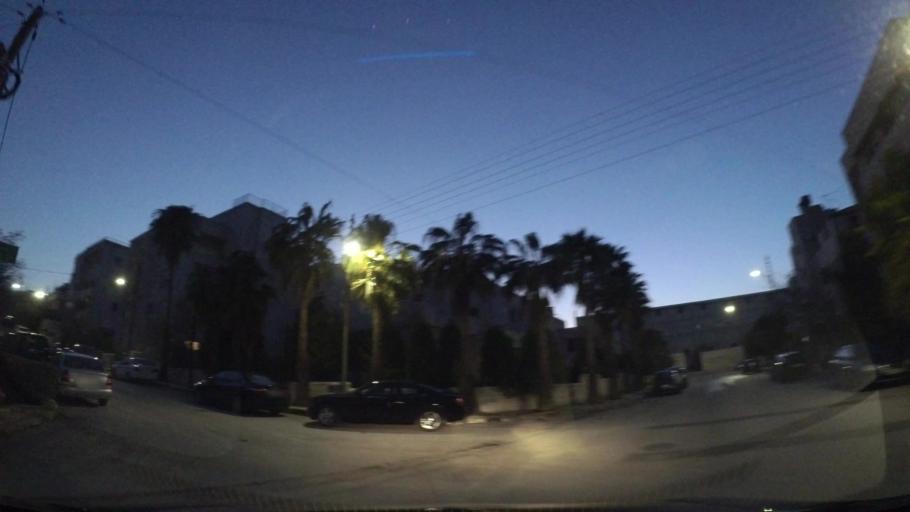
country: JO
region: Amman
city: Al Jubayhah
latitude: 31.9806
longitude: 35.8800
